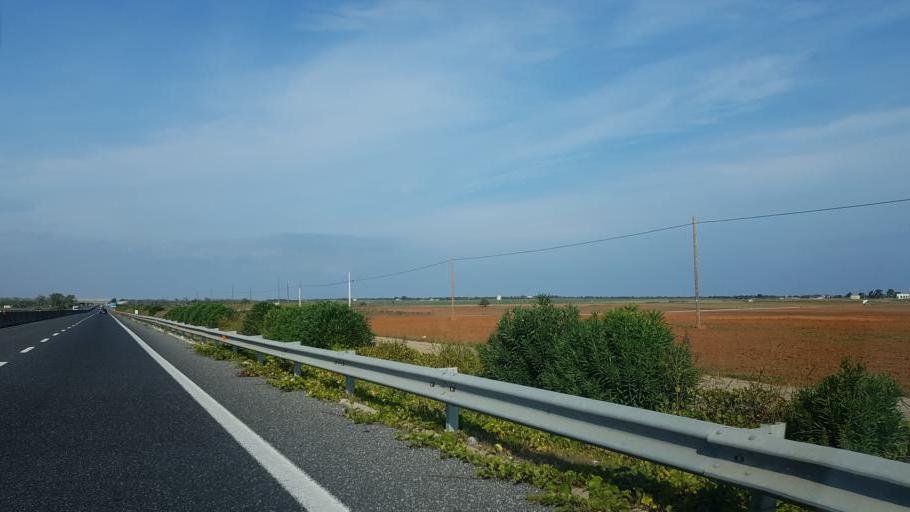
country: IT
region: Apulia
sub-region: Provincia di Brindisi
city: Brindisi
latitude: 40.6719
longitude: 17.8546
